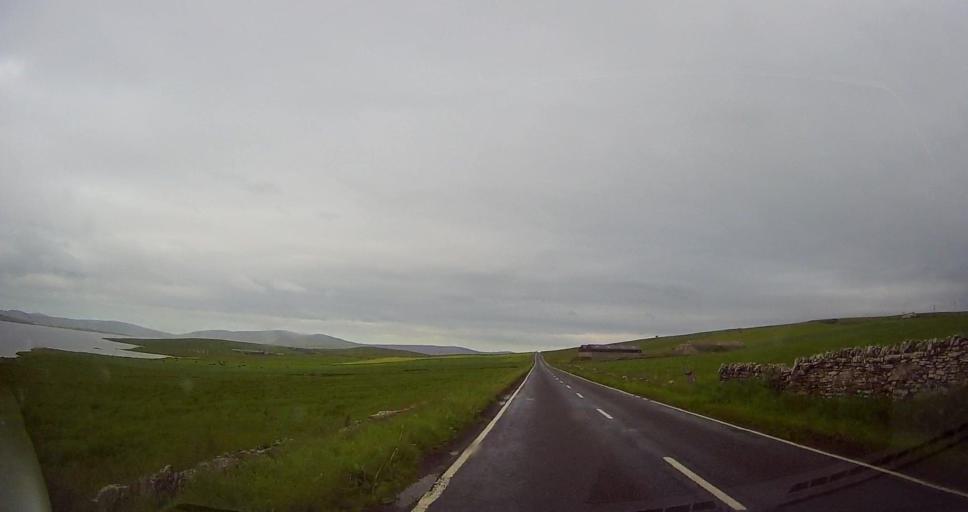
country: GB
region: Scotland
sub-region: Orkney Islands
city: Stromness
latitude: 59.0095
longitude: -3.2946
